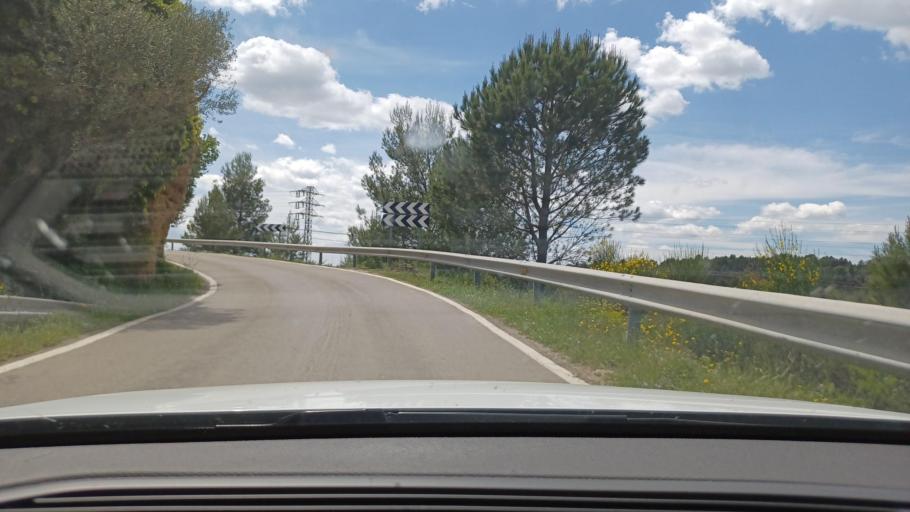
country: ES
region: Valencia
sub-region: Provincia de Castello
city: Rosell
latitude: 40.6467
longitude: 0.2695
